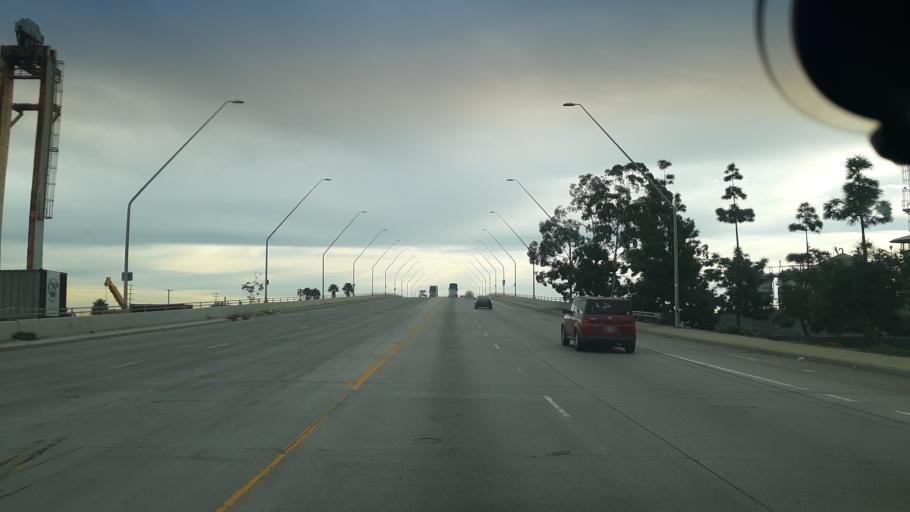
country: US
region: California
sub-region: Los Angeles County
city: Long Beach
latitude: 33.7808
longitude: -118.2421
